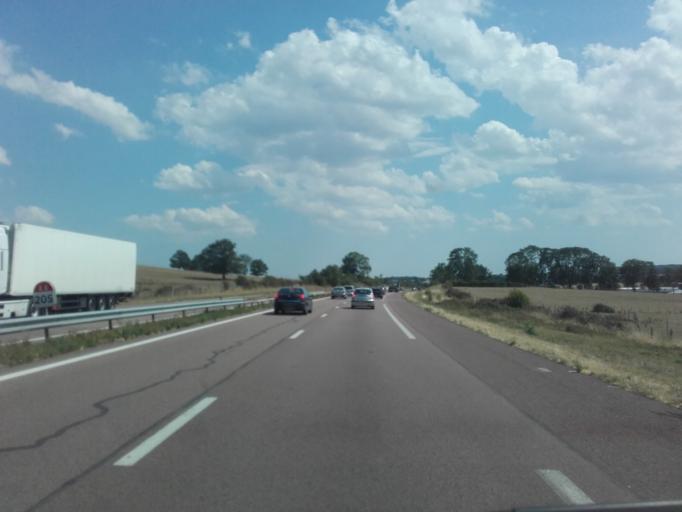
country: FR
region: Bourgogne
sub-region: Departement de l'Yonne
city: Avallon
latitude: 47.5487
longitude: 3.9656
